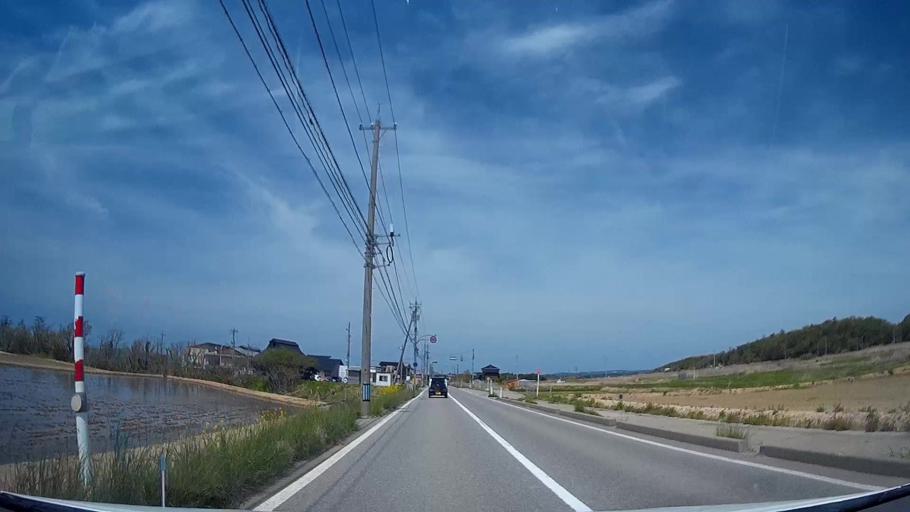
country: JP
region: Ishikawa
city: Hakui
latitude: 36.9382
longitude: 136.7596
